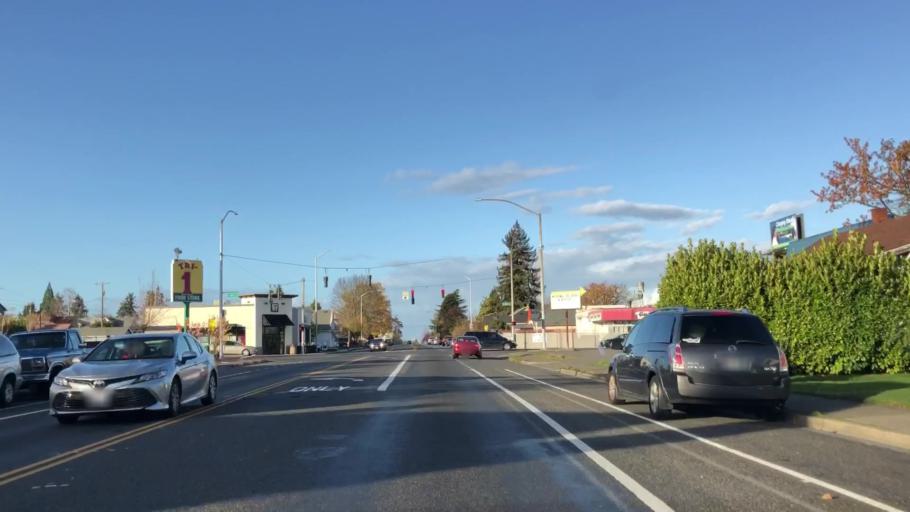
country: US
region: Washington
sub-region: Pierce County
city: Tacoma
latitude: 47.2057
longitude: -122.4432
